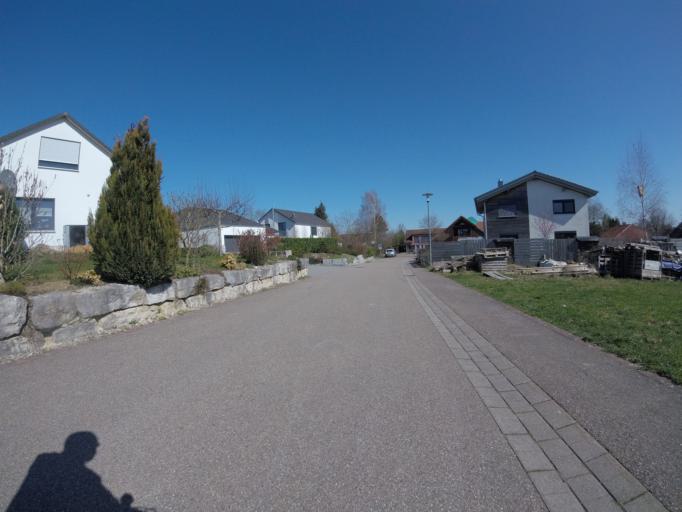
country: DE
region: Baden-Wuerttemberg
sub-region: Regierungsbezirk Stuttgart
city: Durlangen
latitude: 48.8630
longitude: 9.7799
